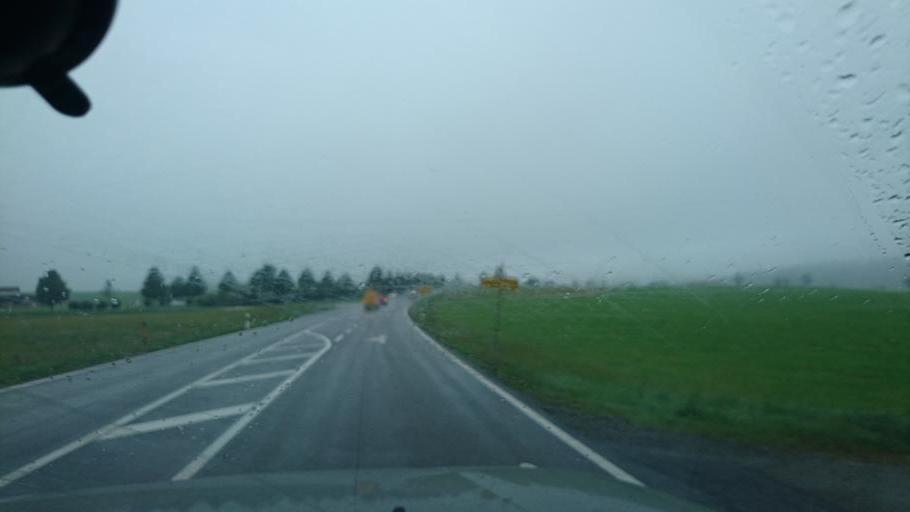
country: DE
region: Baden-Wuerttemberg
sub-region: Karlsruhe Region
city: Baiersbronn
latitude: 48.5851
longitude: 8.4196
